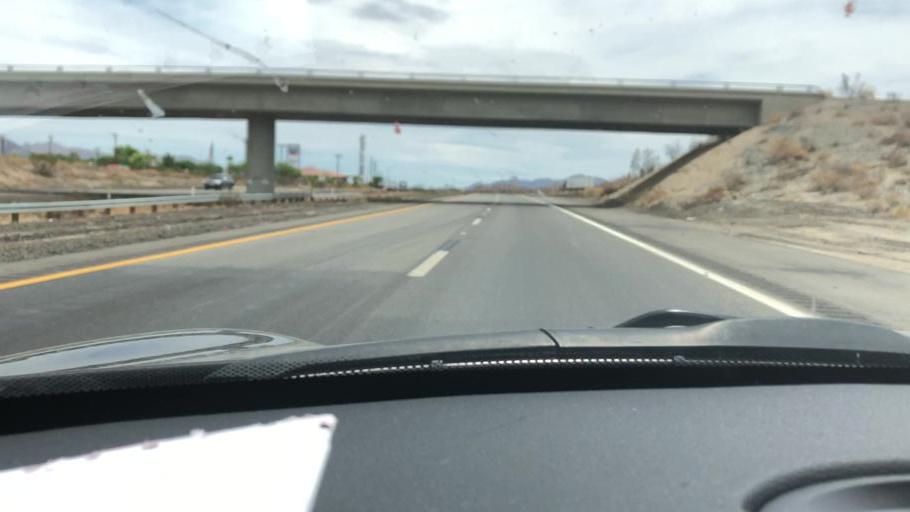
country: US
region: California
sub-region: Riverside County
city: Mecca
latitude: 33.6600
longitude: -115.7244
